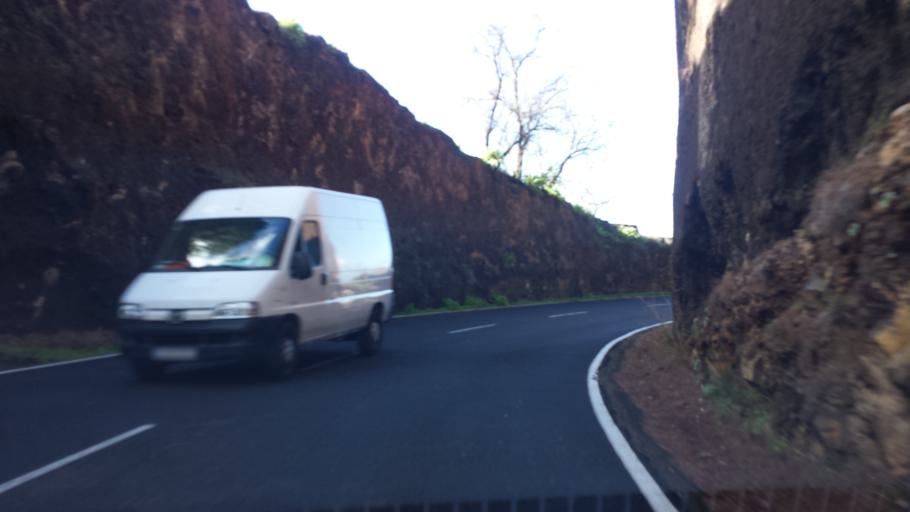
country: ES
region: Canary Islands
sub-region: Provincia de Santa Cruz de Tenerife
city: Puntagorda
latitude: 28.7495
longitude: -17.9683
